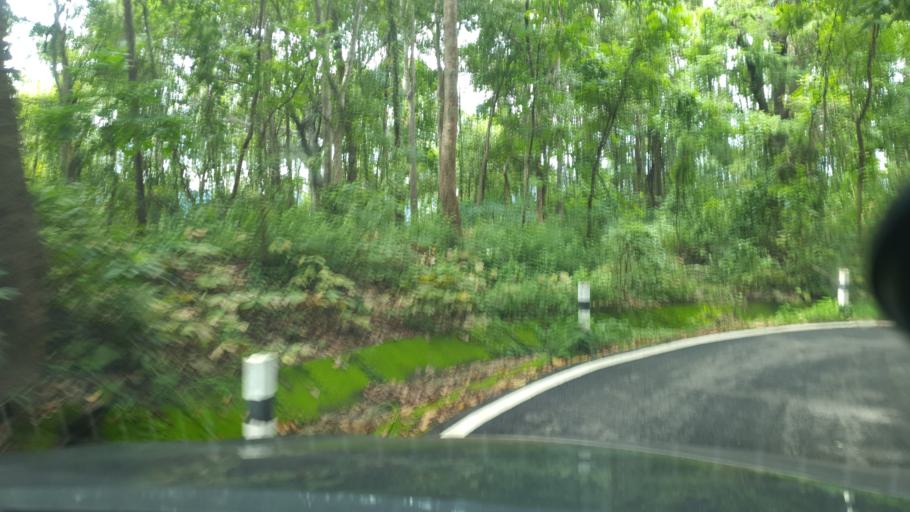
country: TH
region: Lamphun
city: Mae Tha
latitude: 18.4973
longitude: 99.2672
